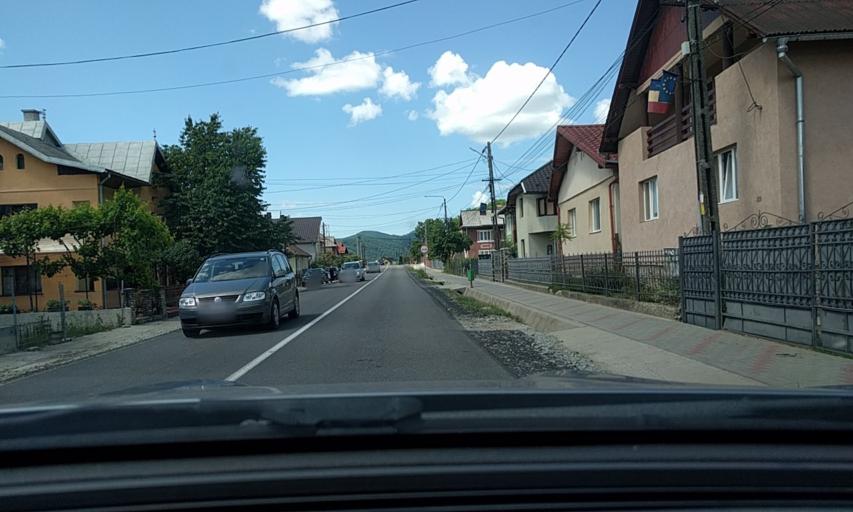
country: RO
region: Bistrita-Nasaud
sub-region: Comuna Rebrisoara
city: Rebrisoara
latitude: 47.2859
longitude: 24.4430
